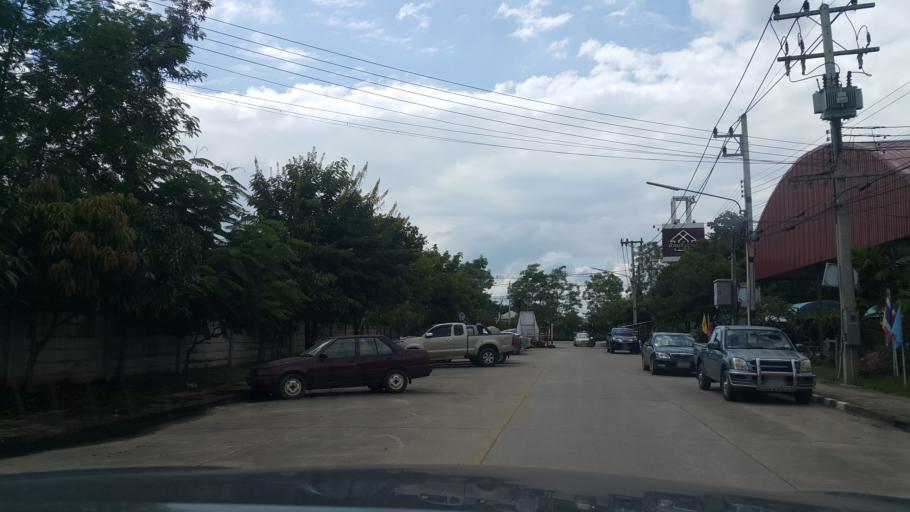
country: TH
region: Chiang Mai
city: Hang Dong
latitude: 18.7335
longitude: 98.9403
